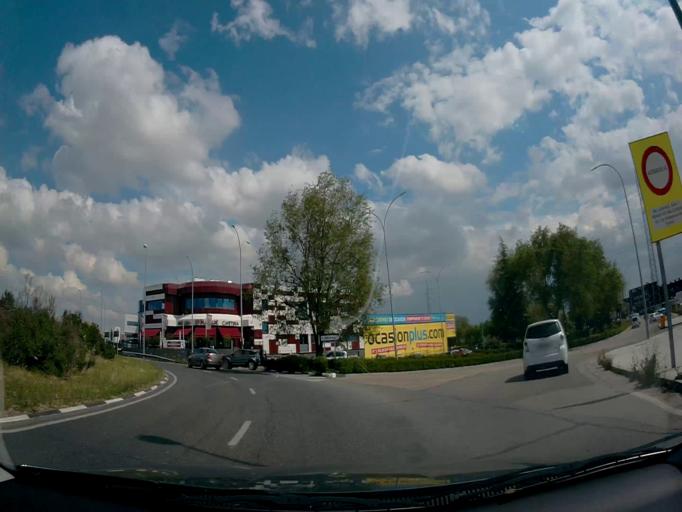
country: ES
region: Madrid
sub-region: Provincia de Madrid
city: Villaviciosa de Odon
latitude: 40.3519
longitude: -3.8816
